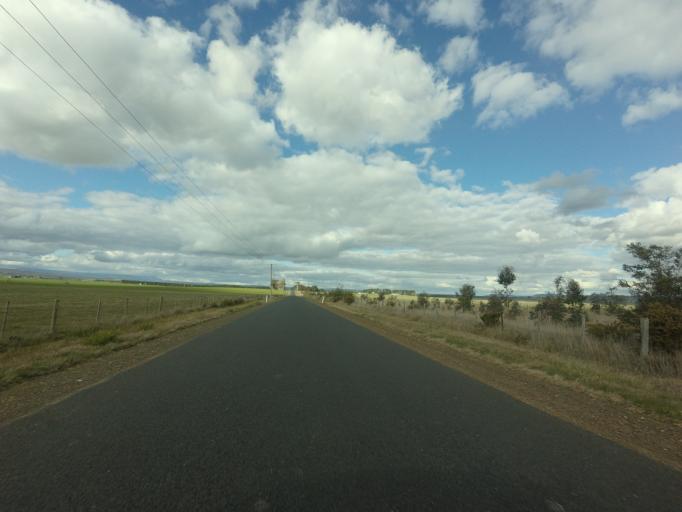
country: AU
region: Tasmania
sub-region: Northern Midlands
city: Longford
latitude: -41.8066
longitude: 147.1683
